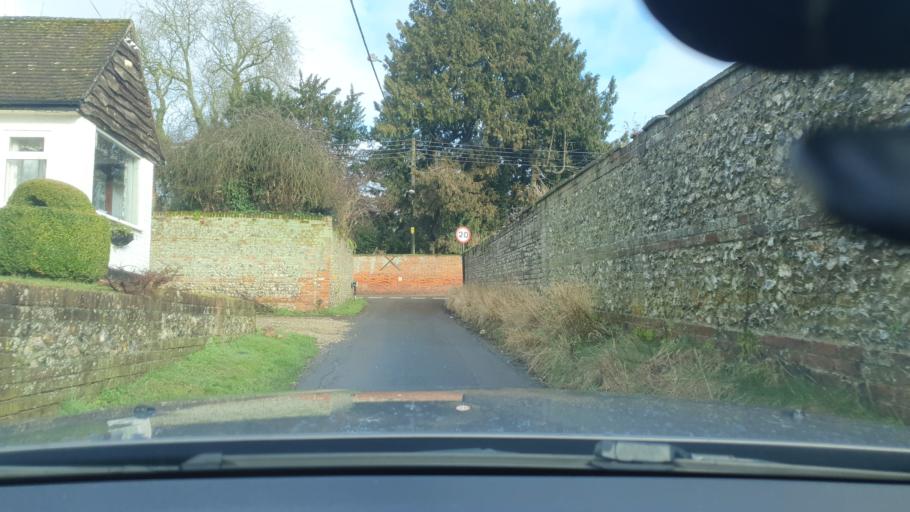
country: GB
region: England
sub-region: Wiltshire
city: Ramsbury
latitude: 51.4430
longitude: -1.6091
